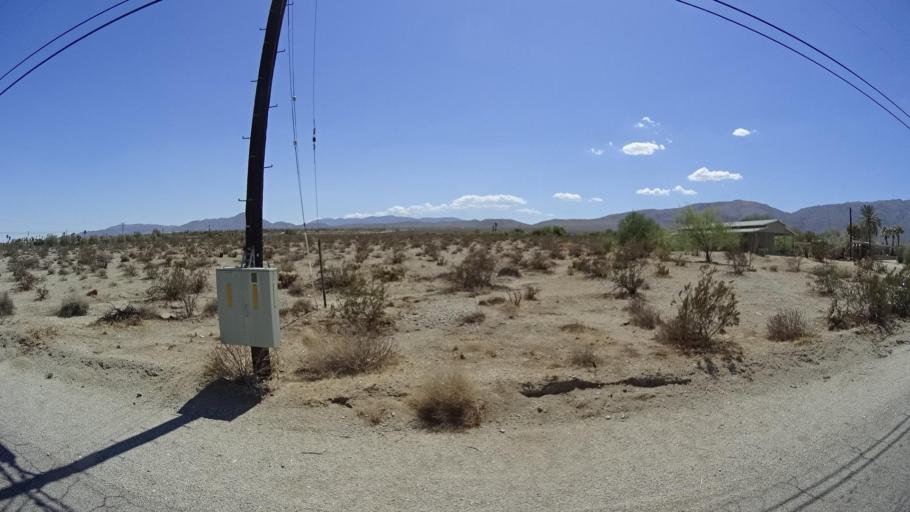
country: US
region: California
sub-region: San Diego County
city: Borrego Springs
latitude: 33.2068
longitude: -116.3313
